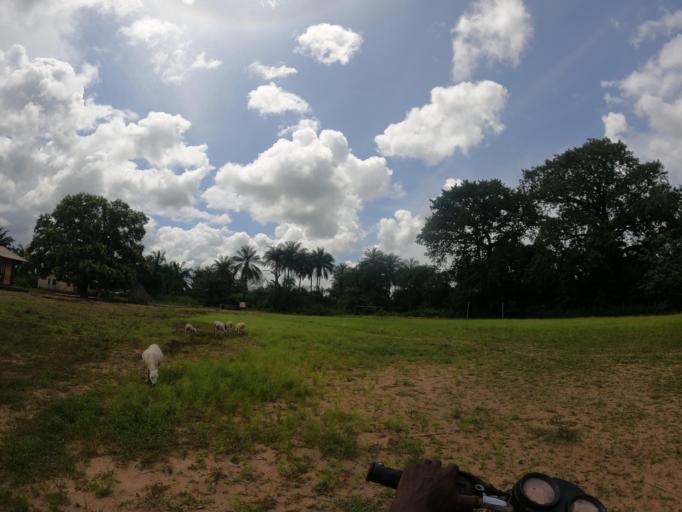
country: SL
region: Northern Province
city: Makeni
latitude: 9.1281
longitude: -12.2691
